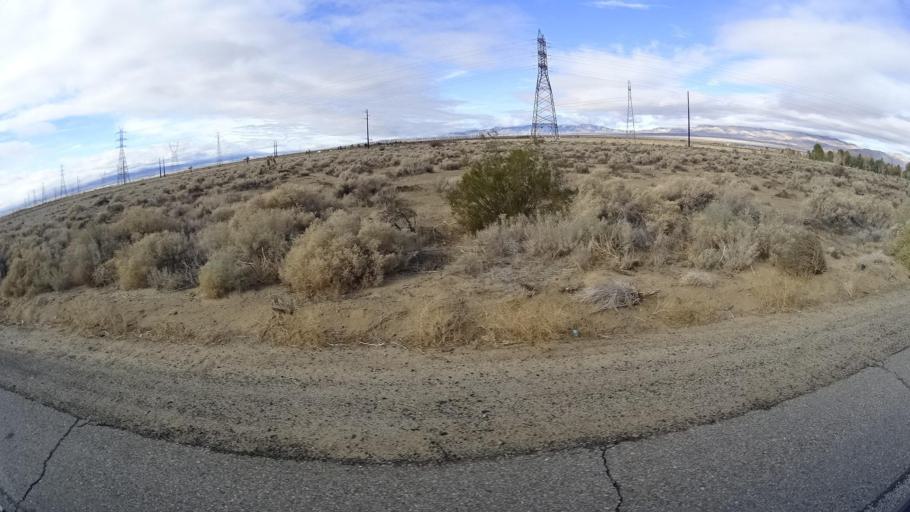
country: US
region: California
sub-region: Kern County
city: Rosamond
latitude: 34.8966
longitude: -118.2912
